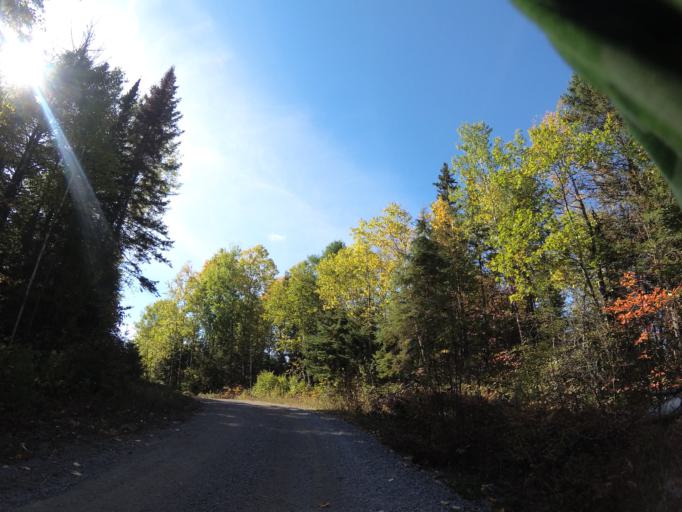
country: CA
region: Ontario
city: Renfrew
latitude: 45.3512
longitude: -77.1335
